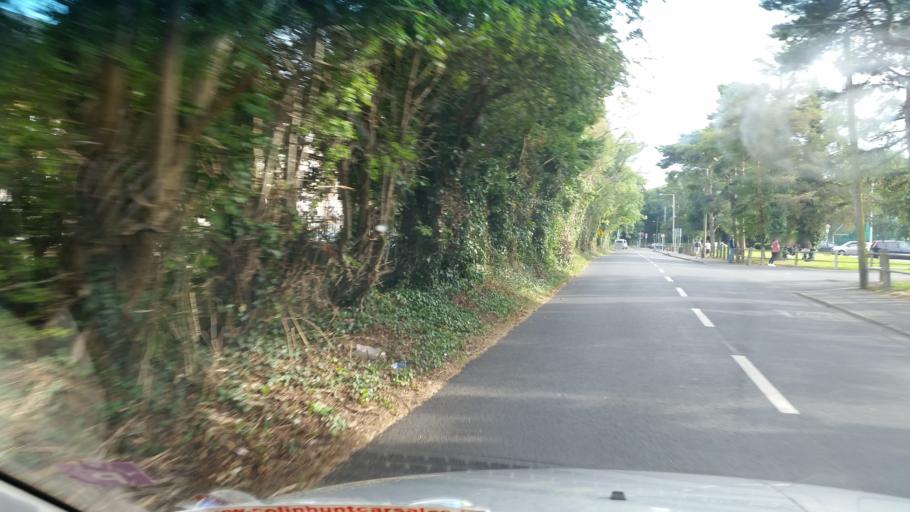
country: IE
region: Leinster
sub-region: Fingal County
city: Blanchardstown
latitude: 53.3879
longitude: -6.3945
